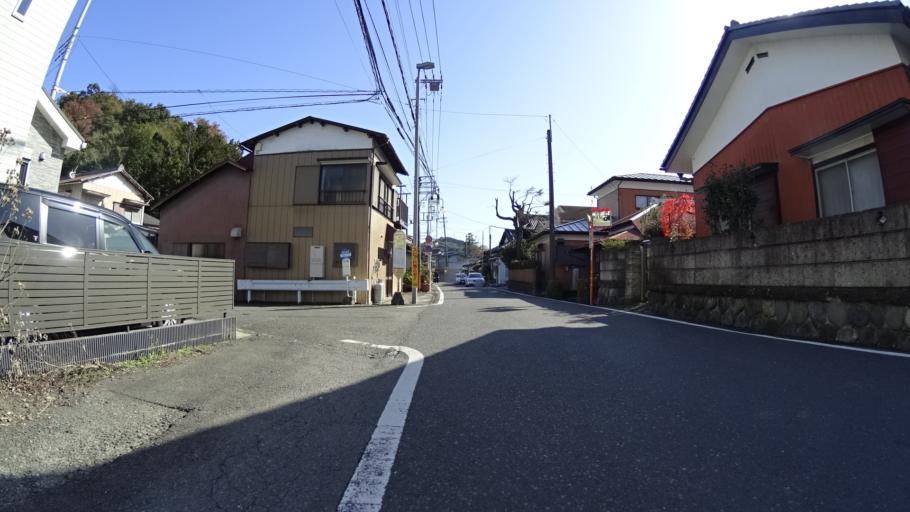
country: JP
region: Kanagawa
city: Zama
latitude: 35.5287
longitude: 139.2868
